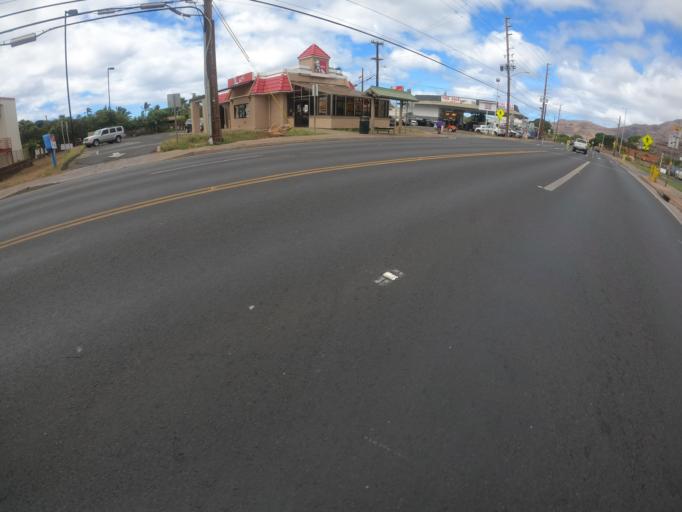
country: US
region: Hawaii
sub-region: Honolulu County
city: Waianae
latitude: 21.4480
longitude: -158.1893
